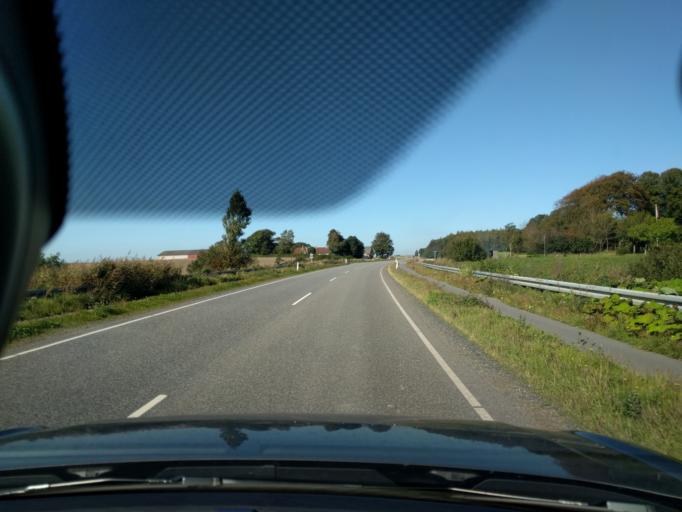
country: DK
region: North Denmark
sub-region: Vesthimmerland Kommune
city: Aars
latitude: 56.7488
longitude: 9.5887
